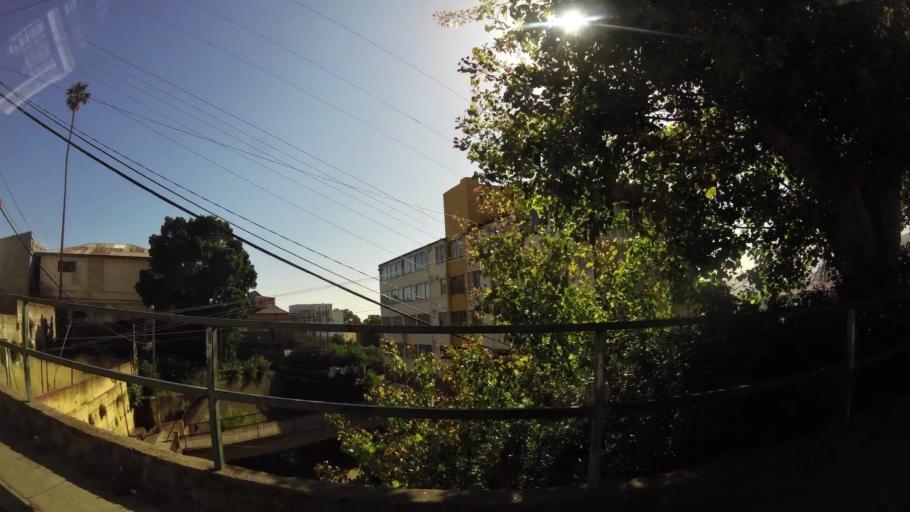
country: CL
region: Valparaiso
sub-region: Provincia de Valparaiso
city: Valparaiso
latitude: -33.0471
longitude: -71.6334
